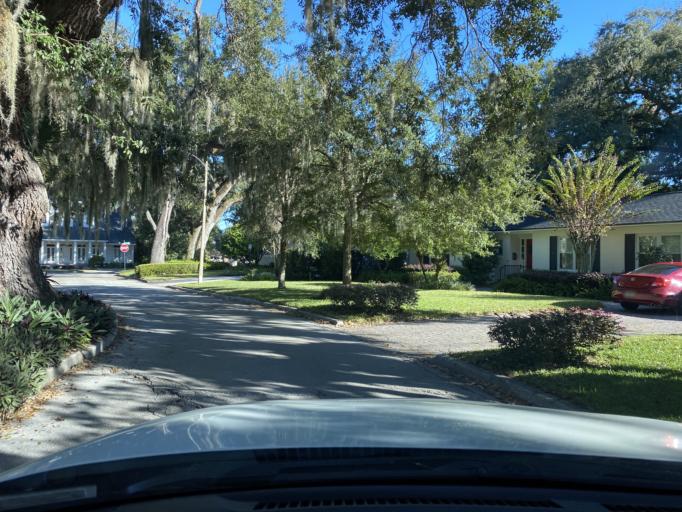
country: US
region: Florida
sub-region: Orange County
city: Orlando
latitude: 28.5564
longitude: -81.4029
